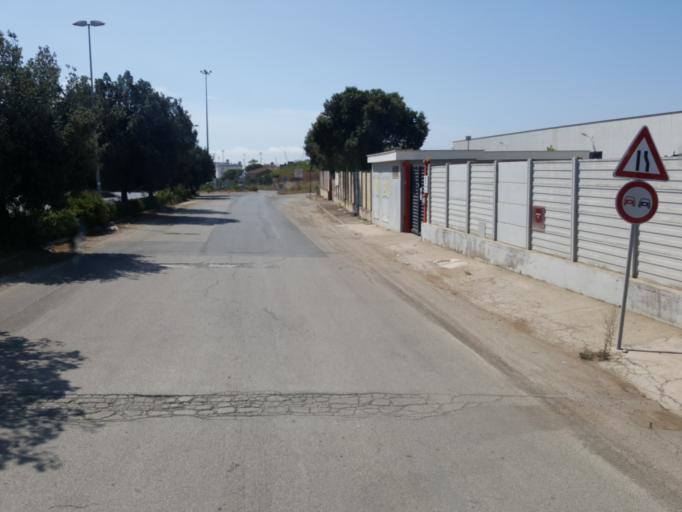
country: IT
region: Latium
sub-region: Citta metropolitana di Roma Capitale
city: Aurelia
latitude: 42.1176
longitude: 11.7787
